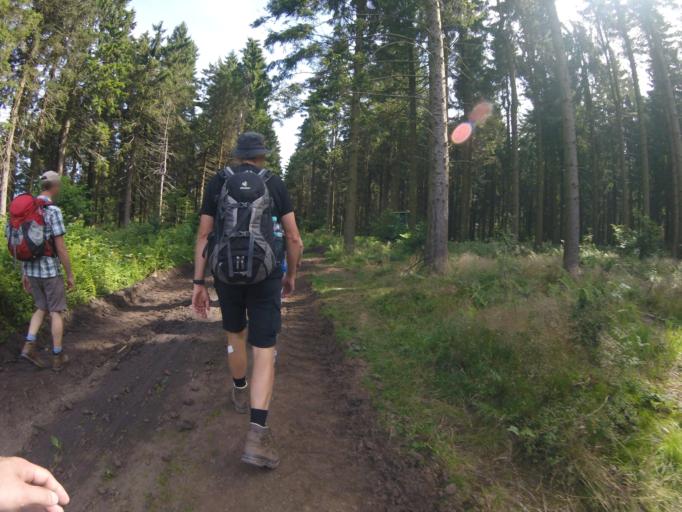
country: DE
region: Hesse
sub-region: Regierungsbezirk Giessen
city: Ulrichstein
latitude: 50.5321
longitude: 9.2415
